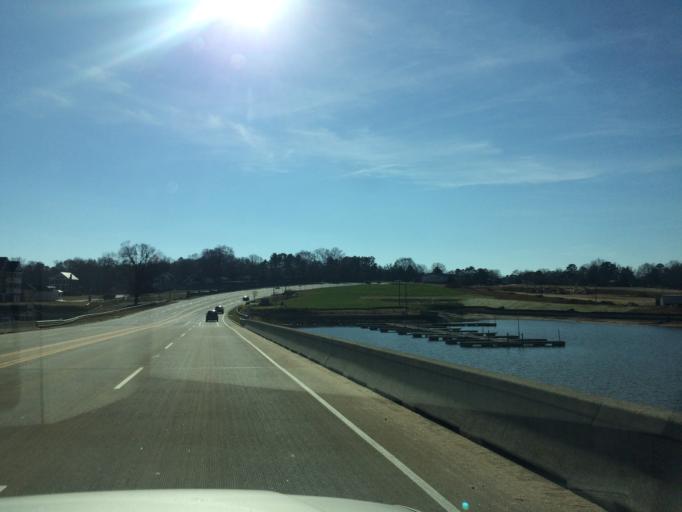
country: US
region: South Carolina
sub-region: Greenwood County
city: Ninety Six
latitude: 34.2798
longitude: -82.0584
